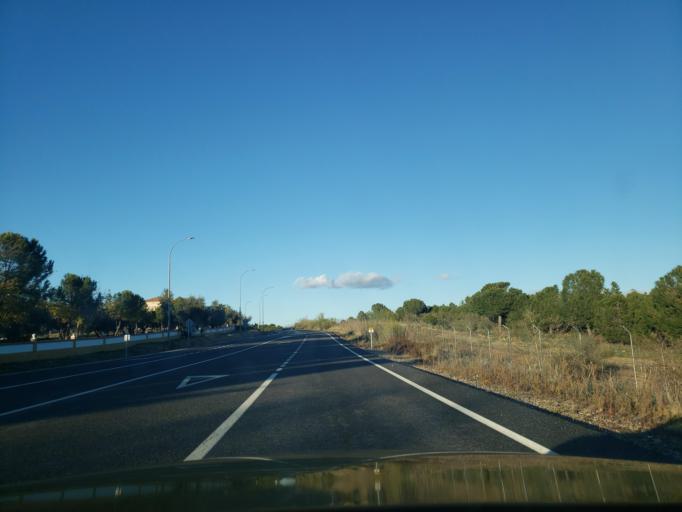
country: ES
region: Castille-La Mancha
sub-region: Province of Toledo
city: Cobisa
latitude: 39.8210
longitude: -4.0188
